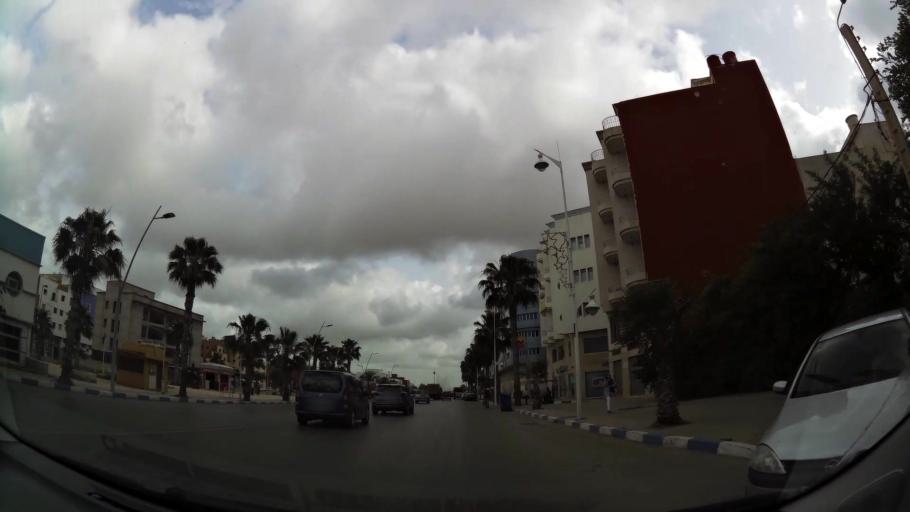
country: MA
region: Oriental
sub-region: Nador
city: Nador
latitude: 35.1538
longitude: -2.9291
